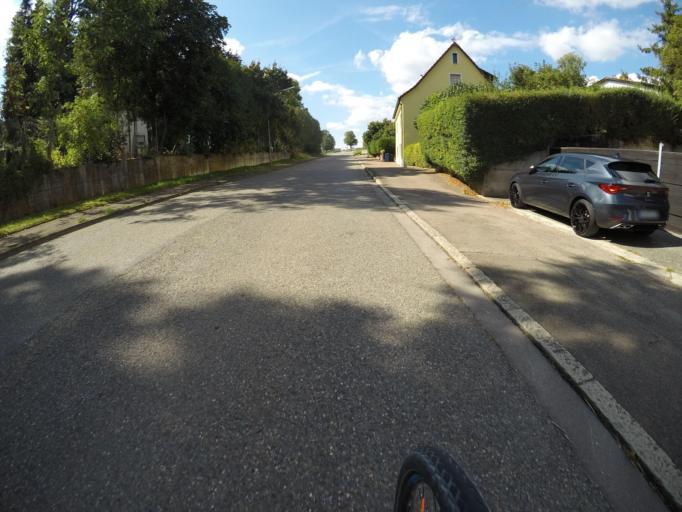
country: DE
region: Bavaria
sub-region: Swabia
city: Bachhagel
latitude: 48.6330
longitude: 10.3176
